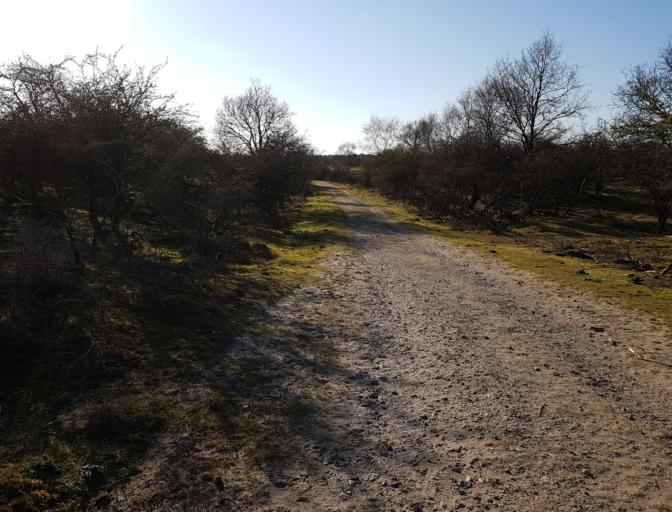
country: NL
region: South Holland
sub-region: Gemeente Hillegom
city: Hillegom
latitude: 52.3127
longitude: 4.5279
